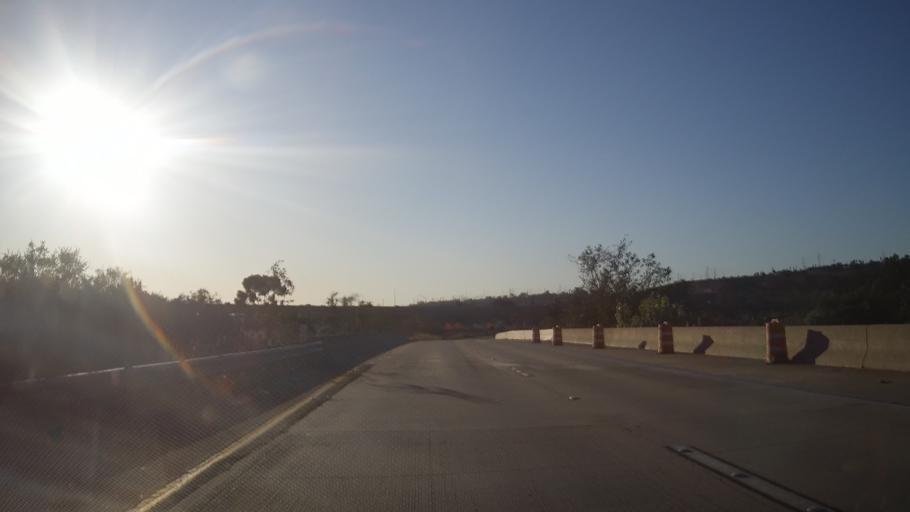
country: US
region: California
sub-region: San Diego County
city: San Diego
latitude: 32.7793
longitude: -117.1094
